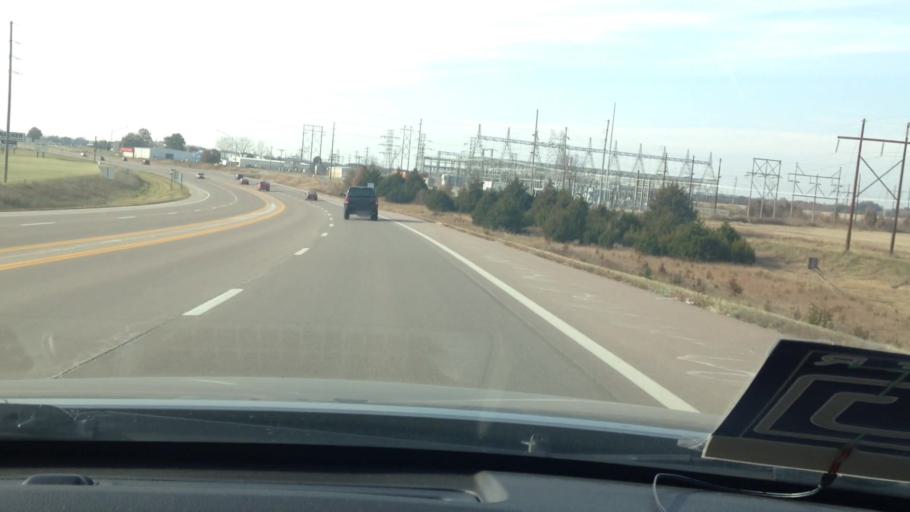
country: US
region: Missouri
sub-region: Henry County
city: Clinton
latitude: 38.3867
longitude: -93.7572
